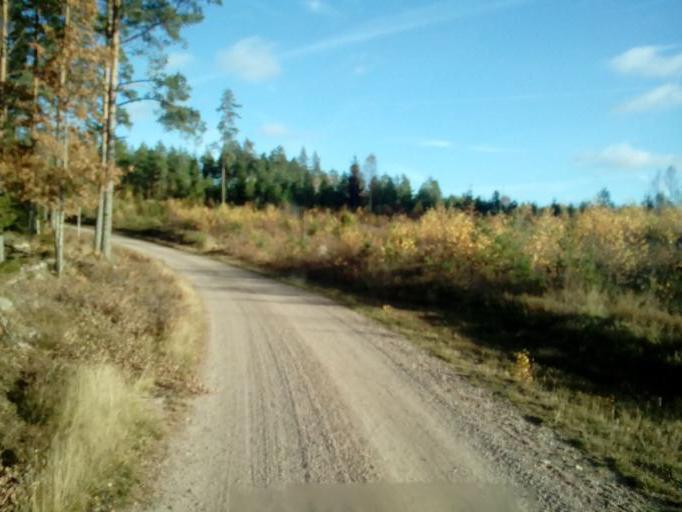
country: SE
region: Kalmar
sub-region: Vimmerby Kommun
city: Vimmerby
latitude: 57.6849
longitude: 15.9224
